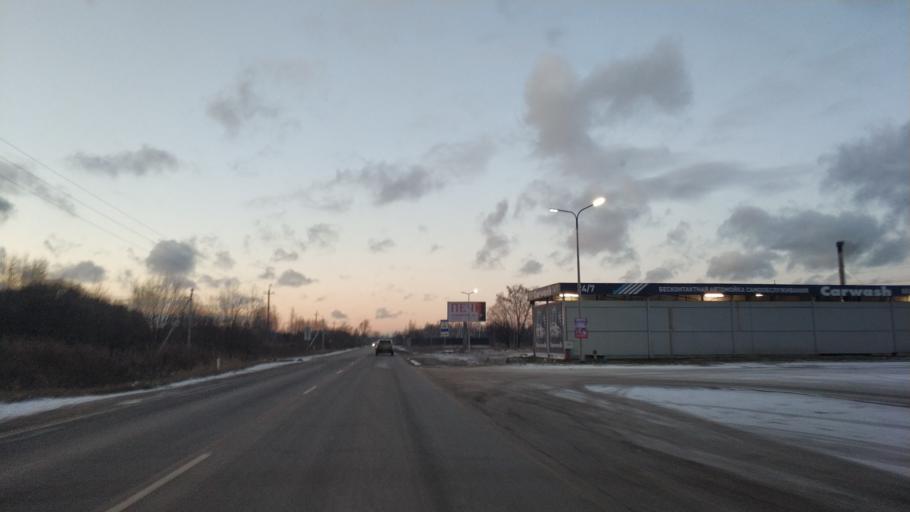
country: RU
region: St.-Petersburg
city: Pontonnyy
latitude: 59.8022
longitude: 30.6320
